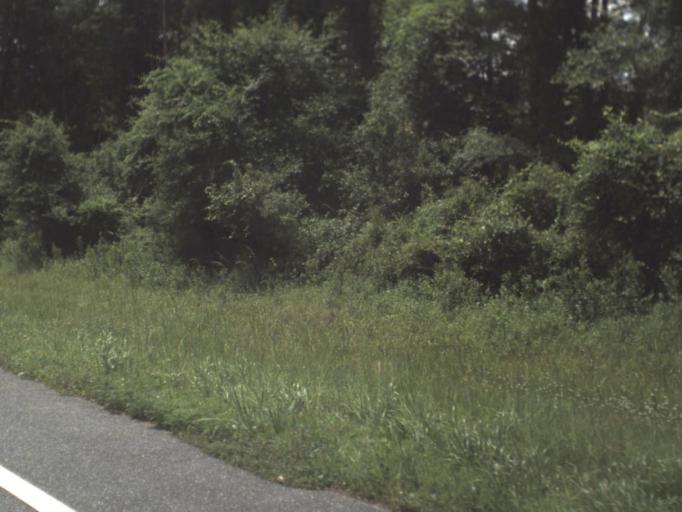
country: US
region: Florida
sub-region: Columbia County
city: Watertown
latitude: 30.1271
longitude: -82.5189
